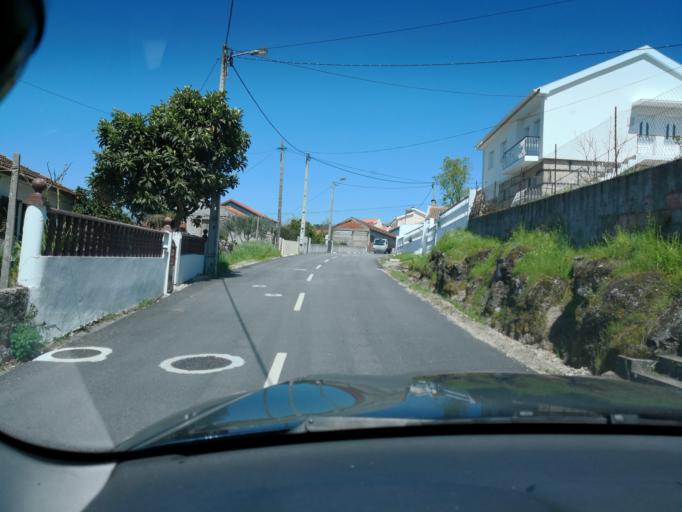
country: PT
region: Vila Real
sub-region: Vila Real
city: Vila Real
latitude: 41.3092
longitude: -7.6968
